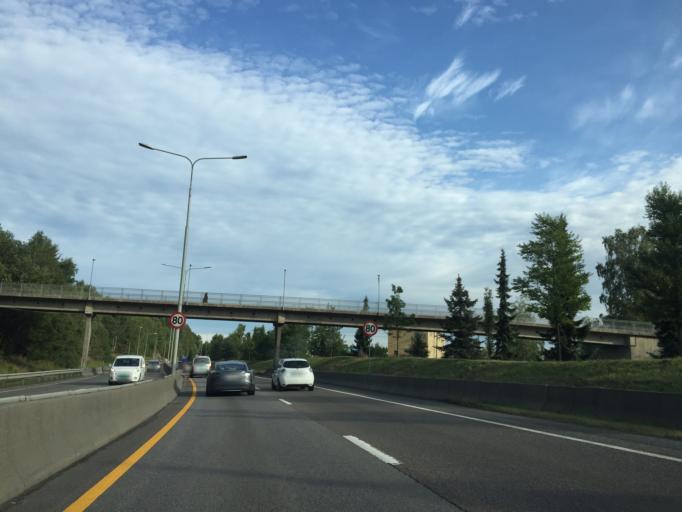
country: NO
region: Akershus
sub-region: Oppegard
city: Kolbotn
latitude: 59.8697
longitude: 10.8289
